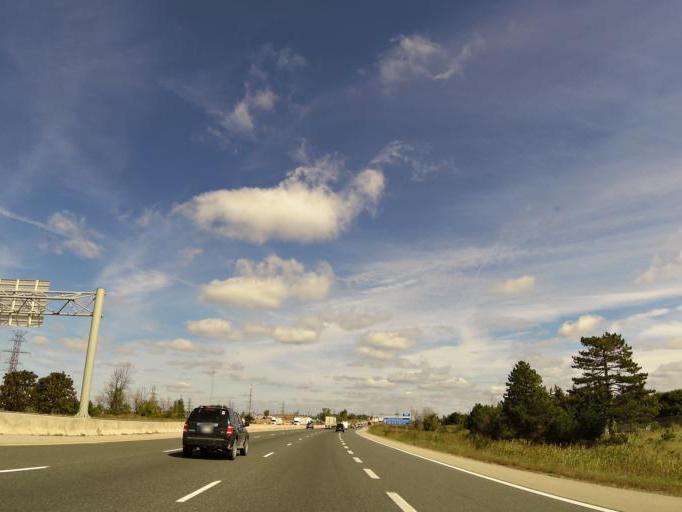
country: CA
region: Ontario
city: London
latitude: 42.9297
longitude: -81.2029
